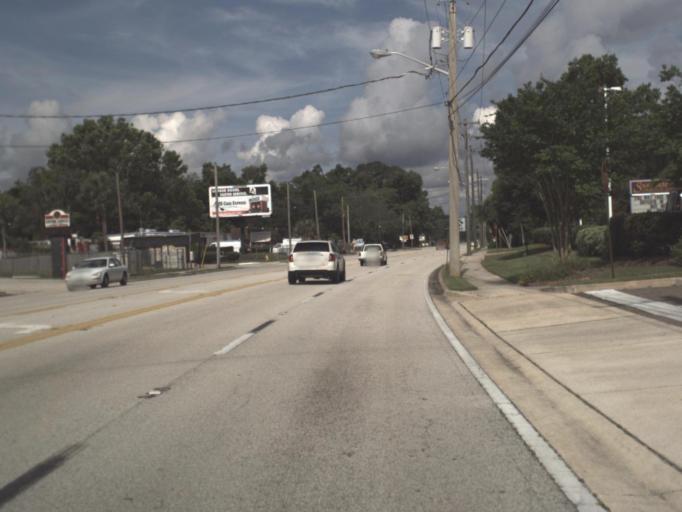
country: US
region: Florida
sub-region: Duval County
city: Jacksonville
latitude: 30.2849
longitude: -81.6399
